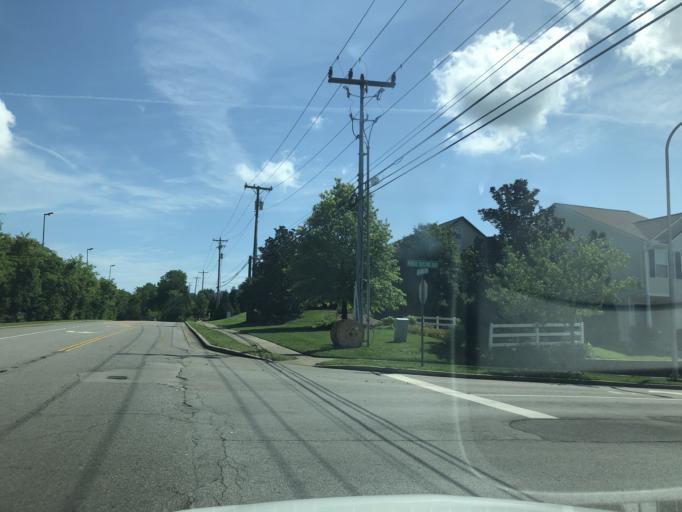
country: US
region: Tennessee
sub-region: Rutherford County
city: La Vergne
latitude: 36.0414
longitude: -86.6323
